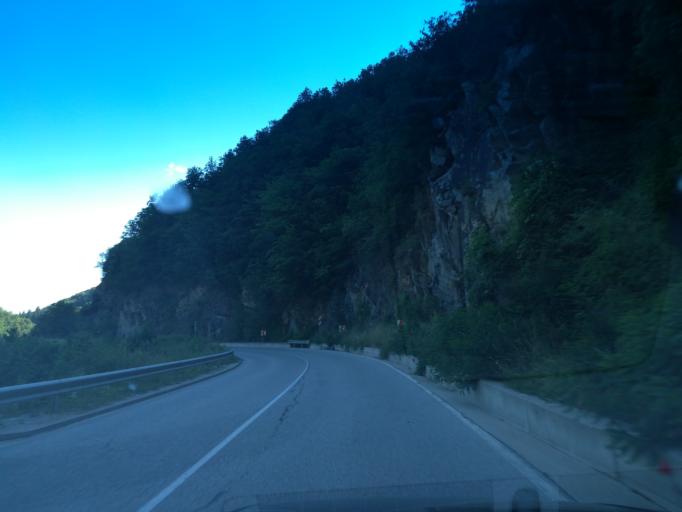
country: BG
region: Smolyan
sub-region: Obshtina Chepelare
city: Chepelare
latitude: 41.7862
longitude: 24.7087
